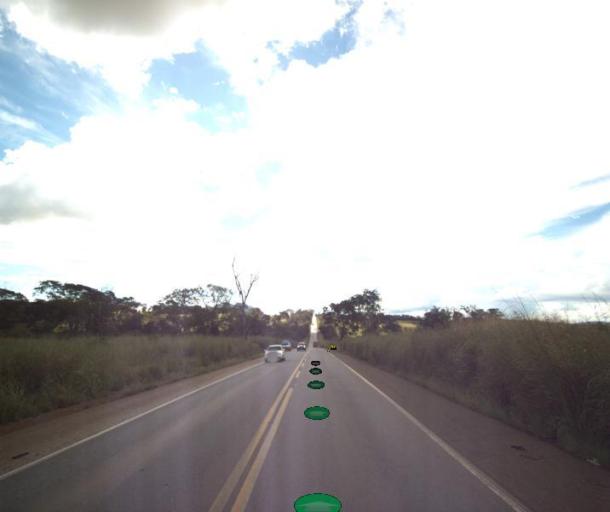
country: BR
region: Goias
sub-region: Jaragua
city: Jaragua
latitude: -15.8679
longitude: -49.2557
